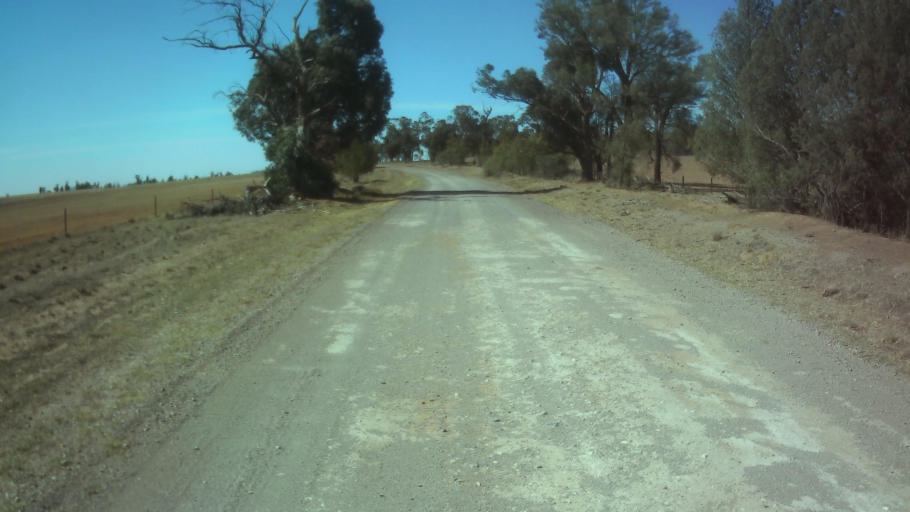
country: AU
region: New South Wales
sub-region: Forbes
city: Forbes
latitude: -33.7160
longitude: 147.7468
